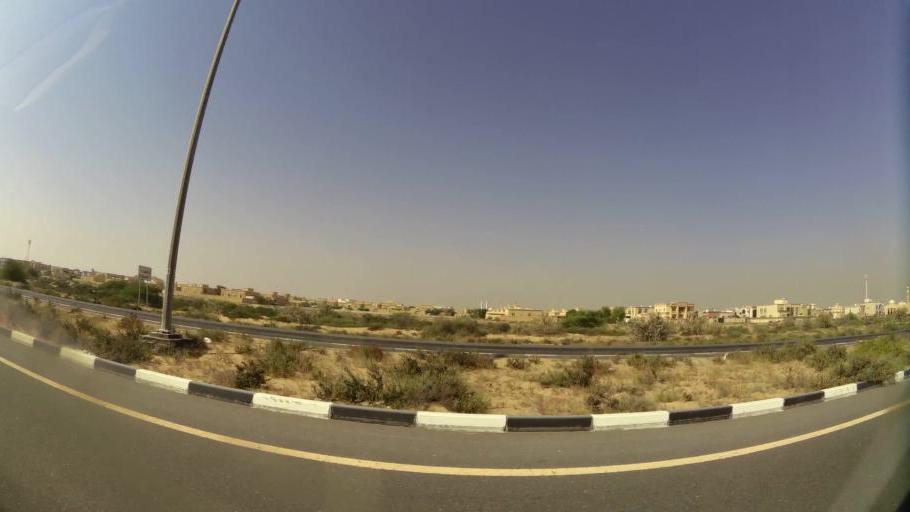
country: AE
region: Ajman
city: Ajman
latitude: 25.4187
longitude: 55.5419
